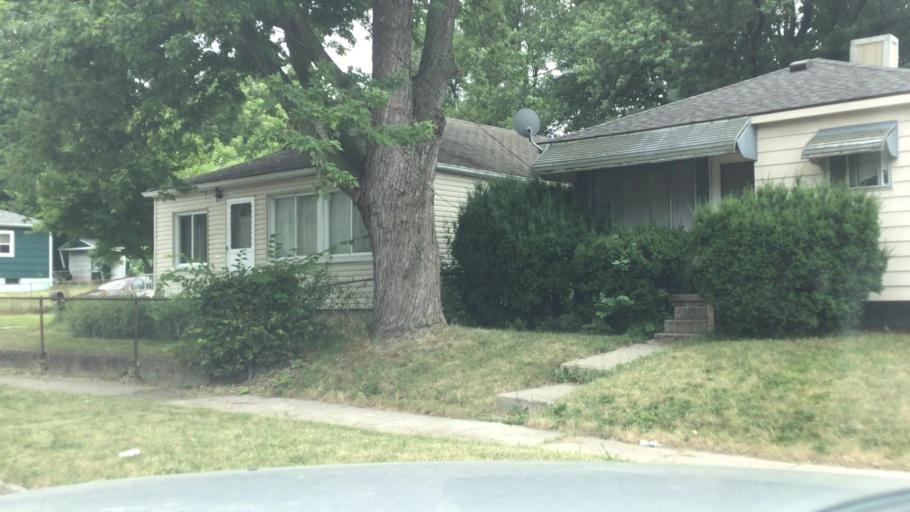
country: US
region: Michigan
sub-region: Genesee County
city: Flint
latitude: 43.0048
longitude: -83.7304
